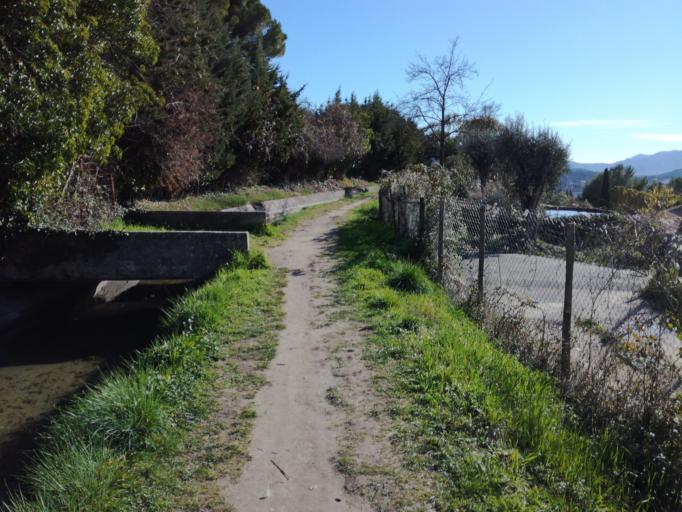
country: FR
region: Provence-Alpes-Cote d'Azur
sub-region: Departement des Alpes-Maritimes
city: Mouans-Sartoux
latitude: 43.6212
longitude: 6.9813
